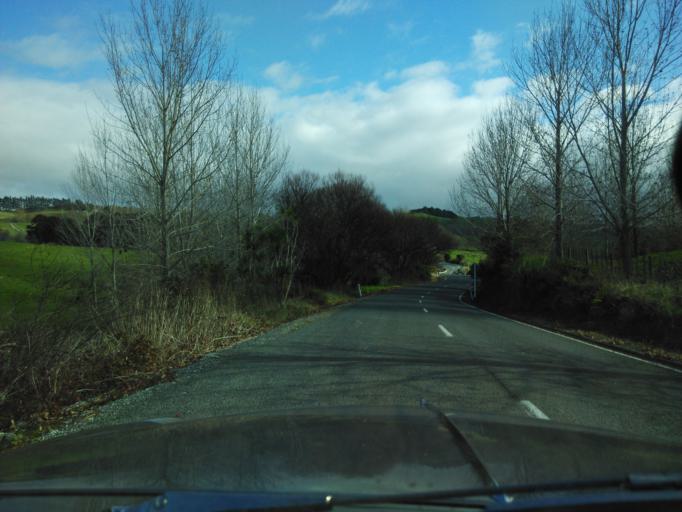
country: NZ
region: Auckland
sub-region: Auckland
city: Wellsford
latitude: -36.1655
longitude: 174.4273
